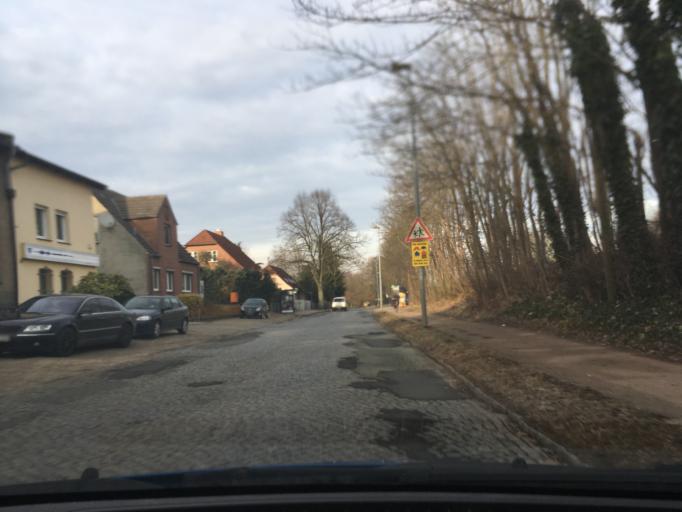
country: DE
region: Mecklenburg-Vorpommern
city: Feldstadt
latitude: 53.6122
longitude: 11.3868
